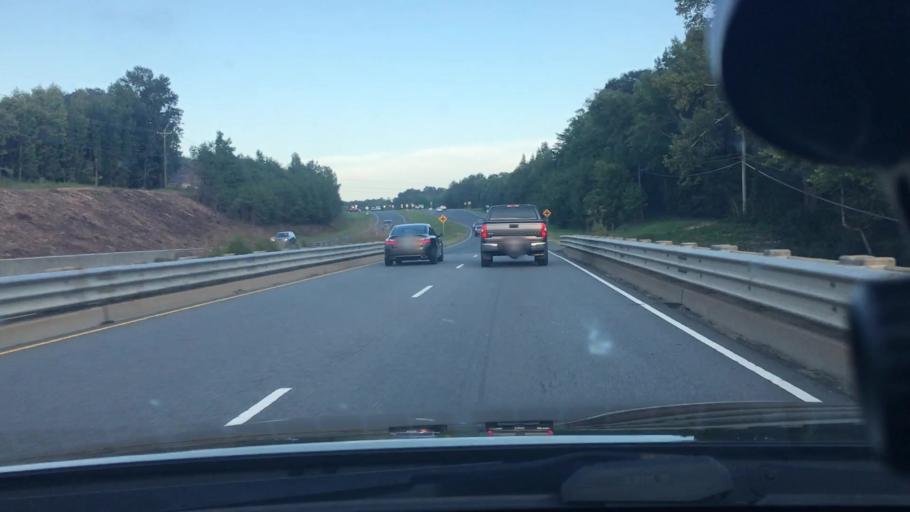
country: US
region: North Carolina
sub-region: Cabarrus County
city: Midland
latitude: 35.2547
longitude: -80.4727
